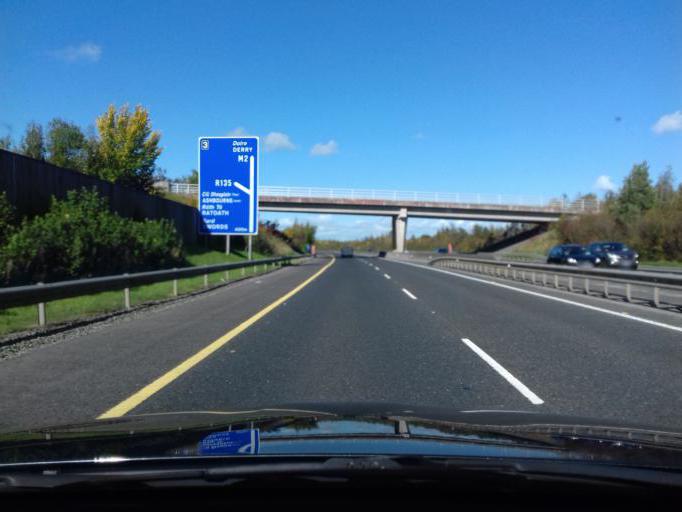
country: IE
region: Leinster
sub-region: An Mhi
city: Ashbourne
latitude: 53.4805
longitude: -6.3736
